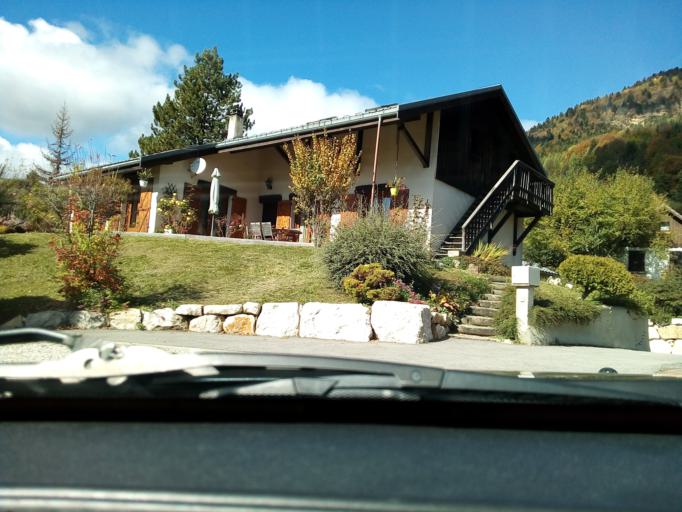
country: FR
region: Rhone-Alpes
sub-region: Departement de l'Isere
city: Le Sappey-en-Chartreuse
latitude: 45.2639
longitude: 5.7782
